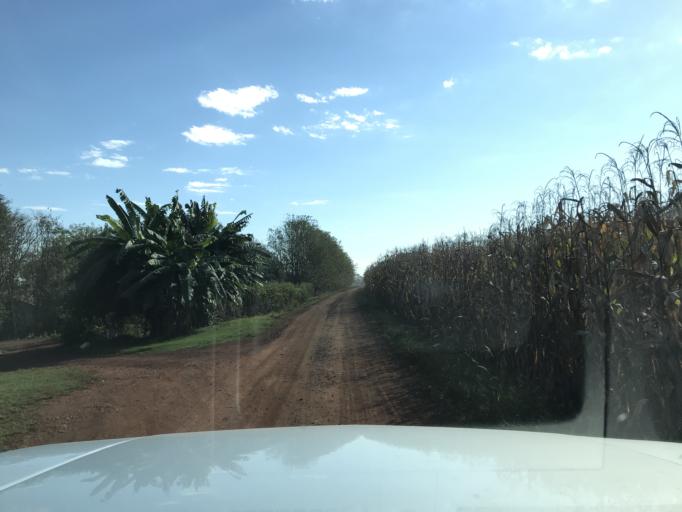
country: BR
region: Parana
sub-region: Palotina
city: Palotina
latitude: -24.2684
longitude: -53.8149
